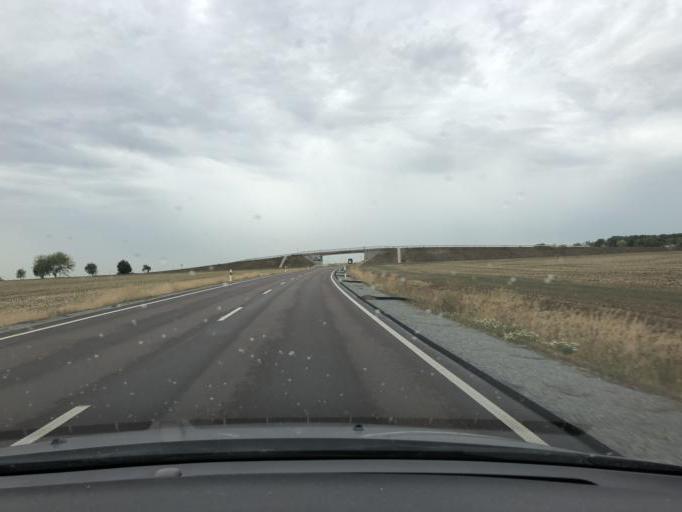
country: DE
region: Saxony-Anhalt
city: Brumby
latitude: 51.8896
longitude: 11.7072
